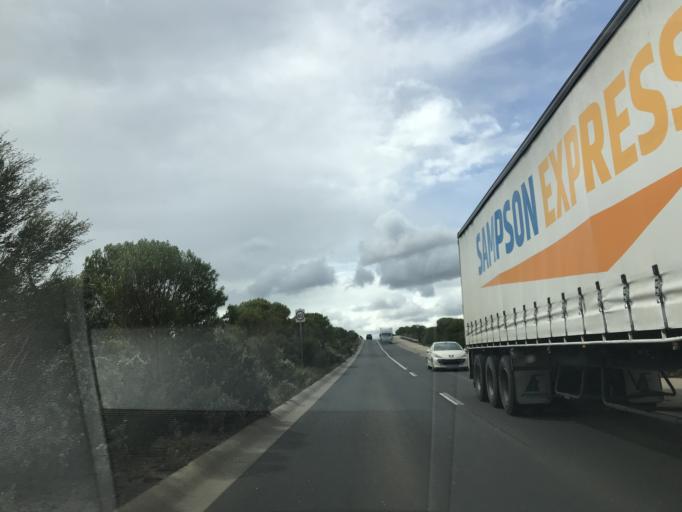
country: AU
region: Victoria
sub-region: Brimbank
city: Derrimut
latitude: -37.8005
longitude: 144.7706
